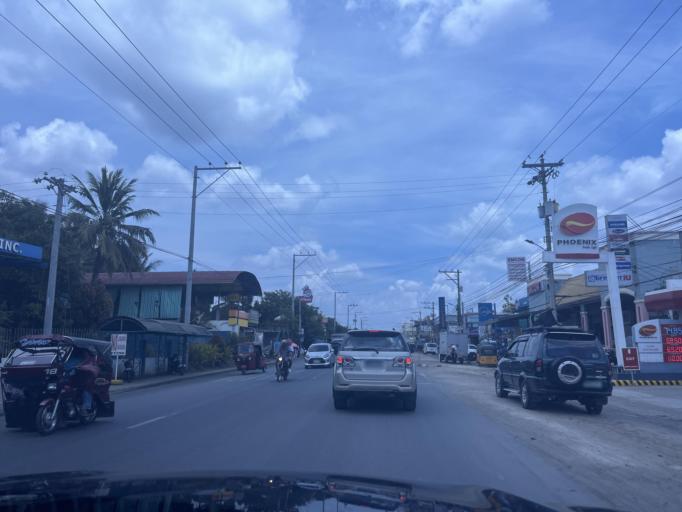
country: PH
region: Davao
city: Lacson
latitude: 7.1886
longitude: 125.4573
